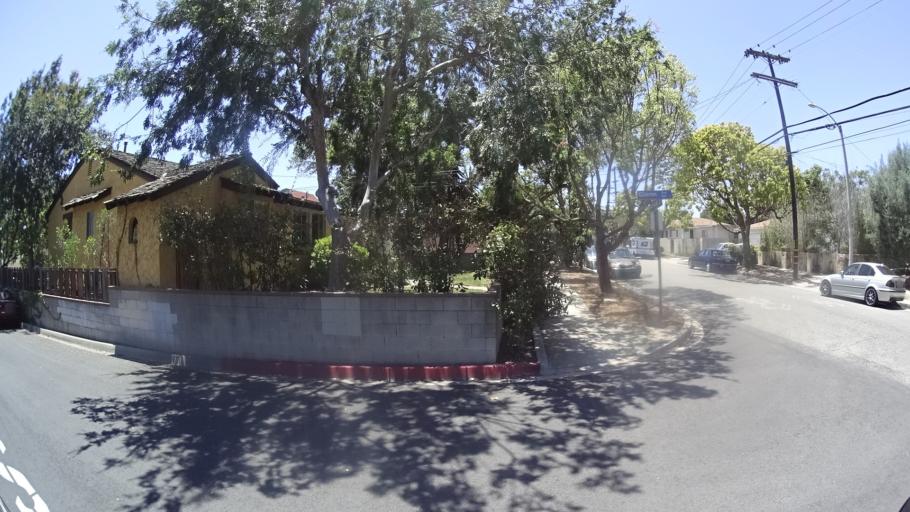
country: US
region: California
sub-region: Los Angeles County
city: Santa Monica
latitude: 34.0065
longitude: -118.4707
